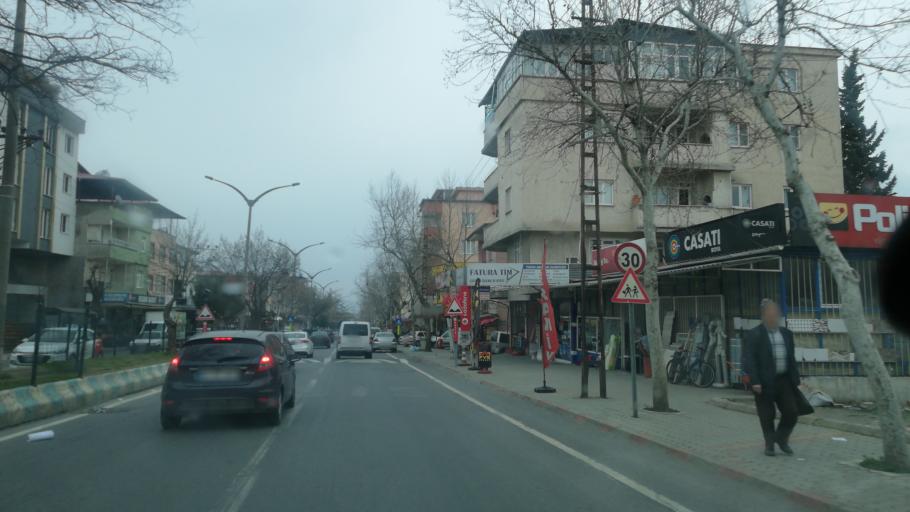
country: TR
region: Kahramanmaras
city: Kahramanmaras
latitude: 37.5690
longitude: 36.9467
